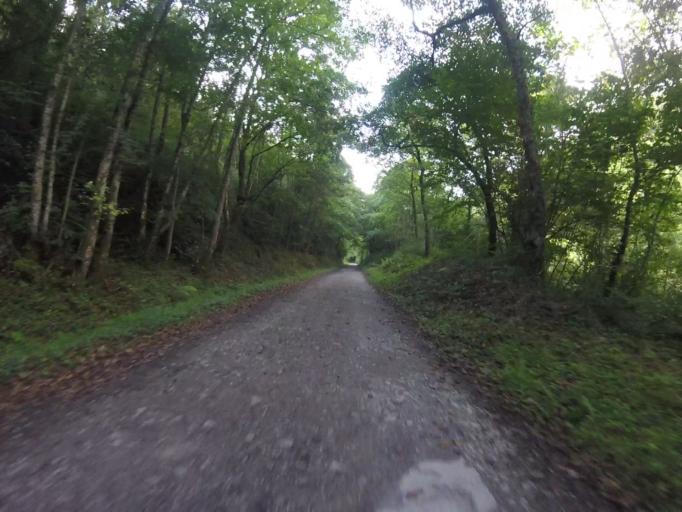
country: ES
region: Basque Country
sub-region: Provincia de Guipuzcoa
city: Elduayen
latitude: 43.1810
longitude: -1.9935
